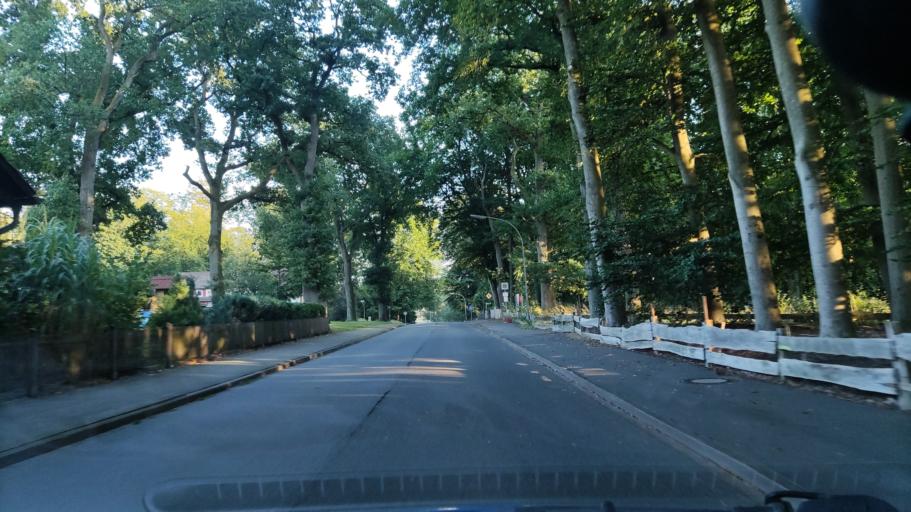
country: DE
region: Lower Saxony
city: Fassberg
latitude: 52.9608
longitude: 10.1849
